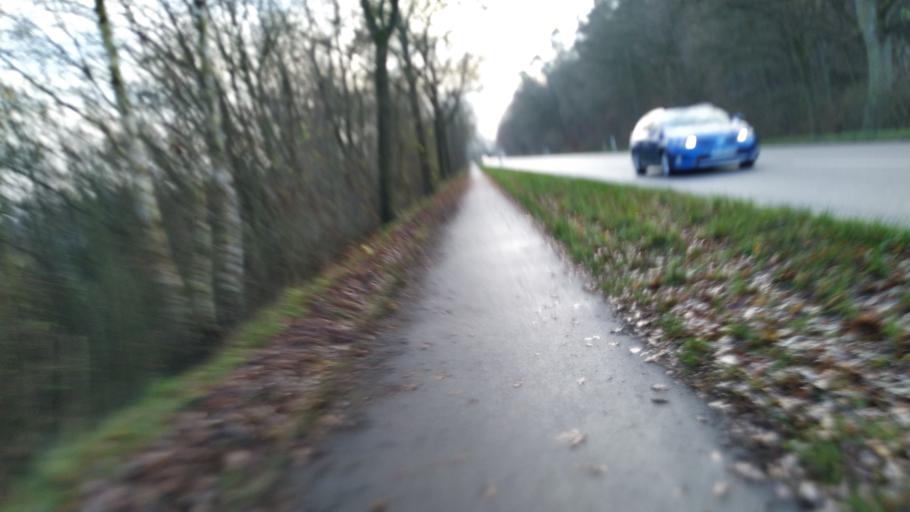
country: DE
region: Schleswig-Holstein
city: Ratekau
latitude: 53.9294
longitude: 10.7373
